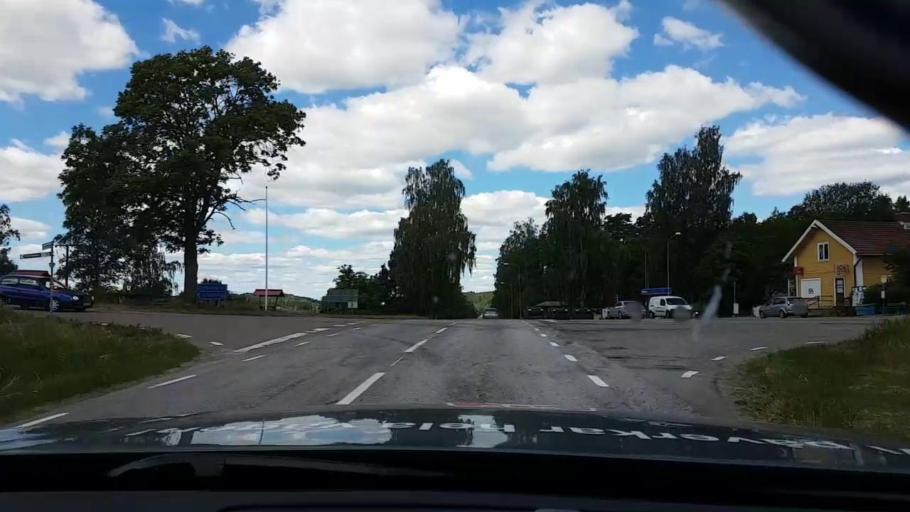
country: SE
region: Kalmar
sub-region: Vasterviks Kommun
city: Overum
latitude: 58.0796
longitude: 16.3543
